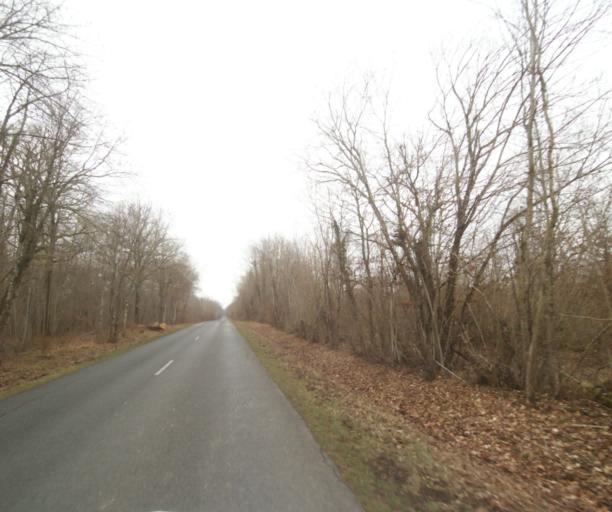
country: FR
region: Champagne-Ardenne
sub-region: Departement de la Haute-Marne
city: Villiers-en-Lieu
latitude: 48.7211
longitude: 4.8759
